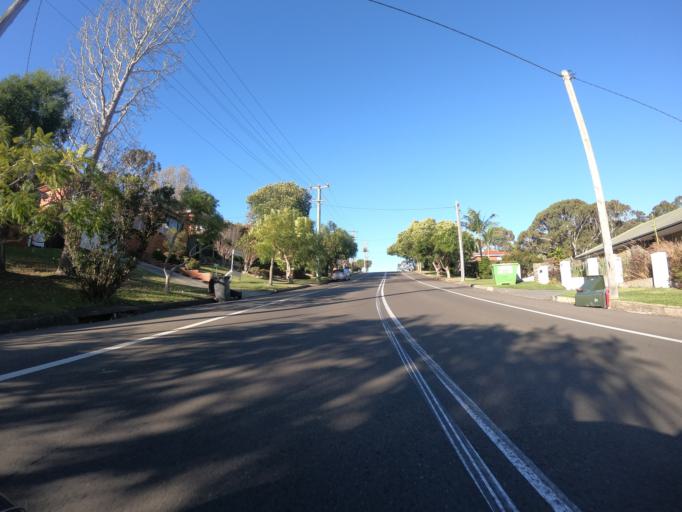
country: AU
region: New South Wales
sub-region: Wollongong
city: Mount Keira
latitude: -34.4241
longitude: 150.8489
